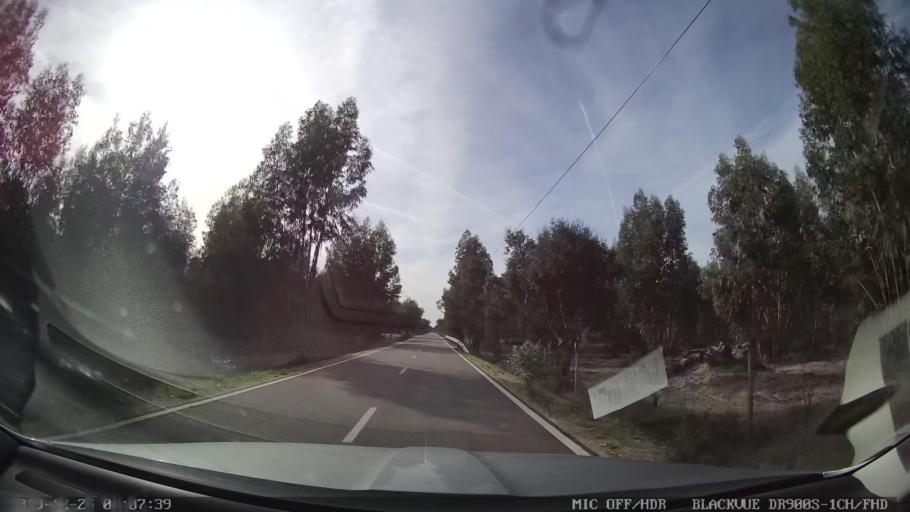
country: PT
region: Portalegre
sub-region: Nisa
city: Nisa
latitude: 39.4598
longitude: -7.7042
